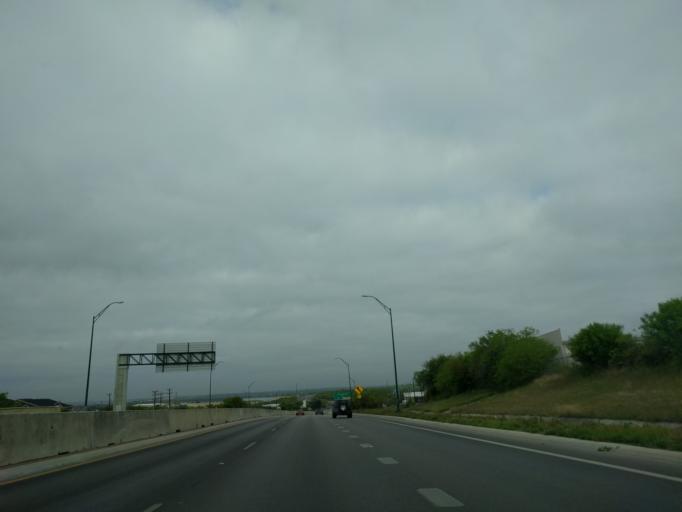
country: US
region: Texas
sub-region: Bexar County
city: Windcrest
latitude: 29.5372
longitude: -98.4164
